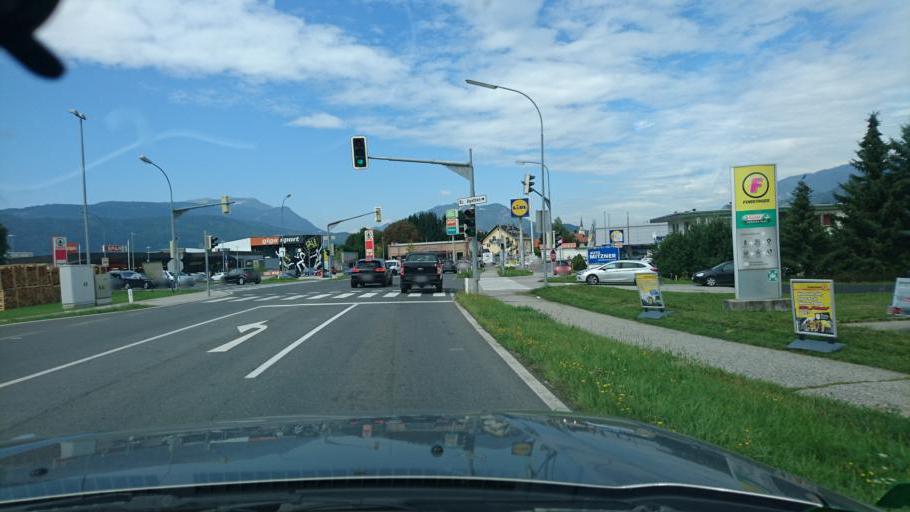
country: AT
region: Carinthia
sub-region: Villach Stadt
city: Villach
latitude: 46.6052
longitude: 13.8629
